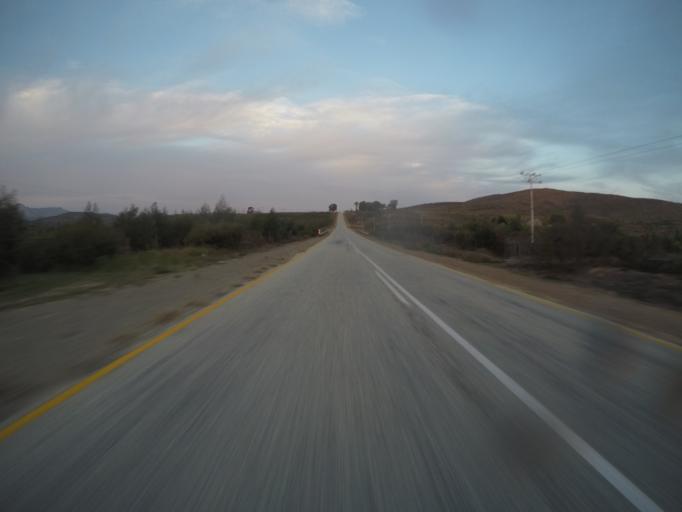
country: ZA
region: Western Cape
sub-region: Eden District Municipality
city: Plettenberg Bay
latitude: -33.7395
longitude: 23.4296
